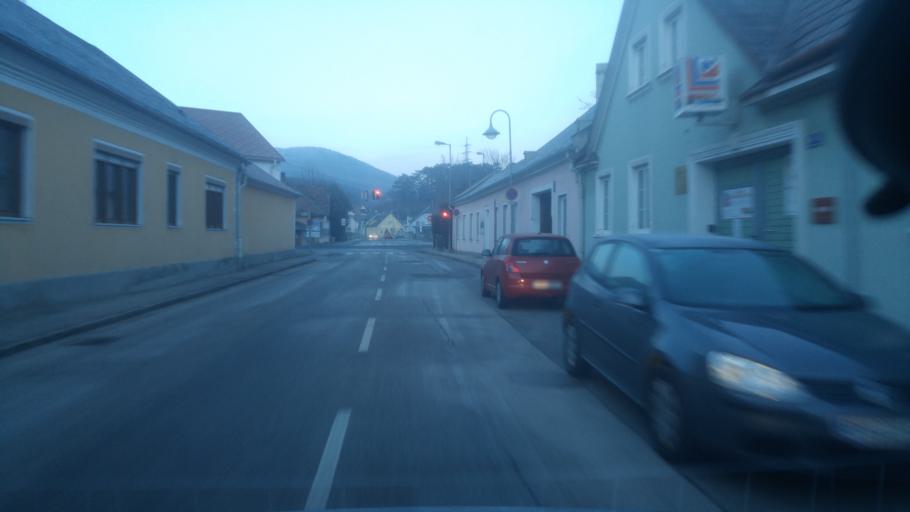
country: AT
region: Lower Austria
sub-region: Politischer Bezirk Baden
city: Pottenstein
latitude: 47.9582
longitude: 16.0943
